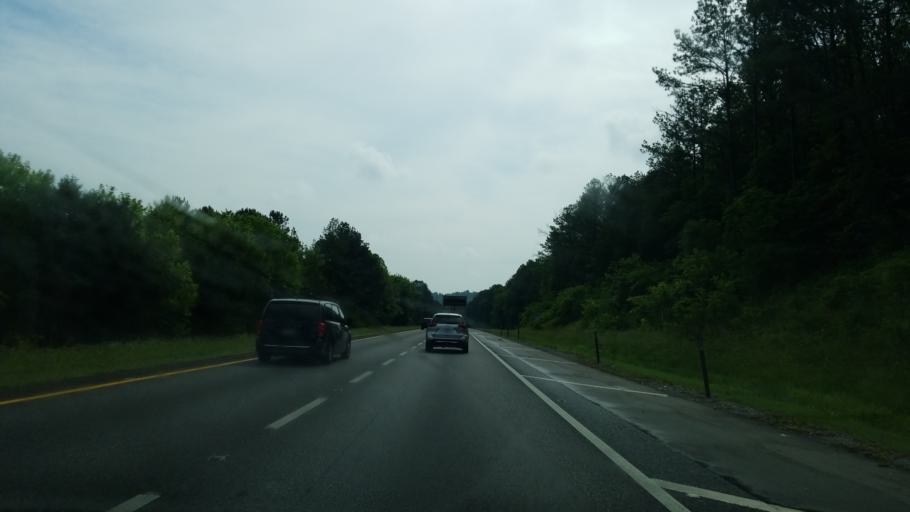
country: US
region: Tennessee
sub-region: Bradley County
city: Hopewell
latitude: 35.3259
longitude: -84.7741
